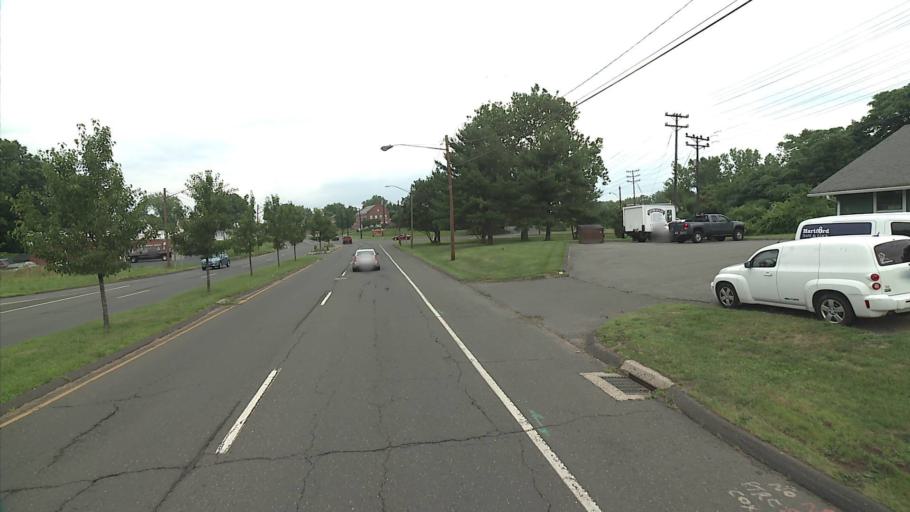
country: US
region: Connecticut
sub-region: Hartford County
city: Wethersfield
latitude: 41.7273
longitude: -72.6682
